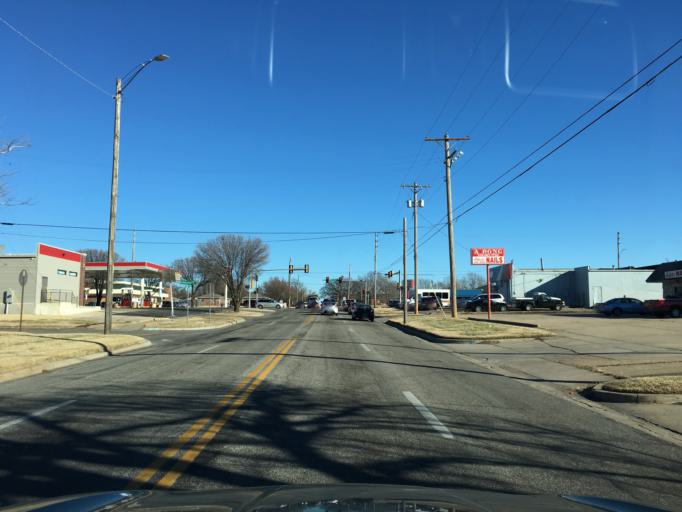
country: US
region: Kansas
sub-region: Sedgwick County
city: Wichita
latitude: 37.6719
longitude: -97.2635
